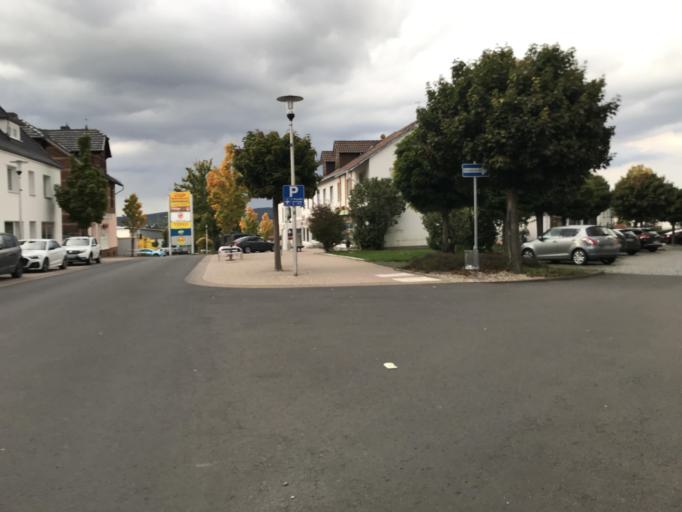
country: DE
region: Hesse
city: Borken
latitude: 51.0482
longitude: 9.2781
